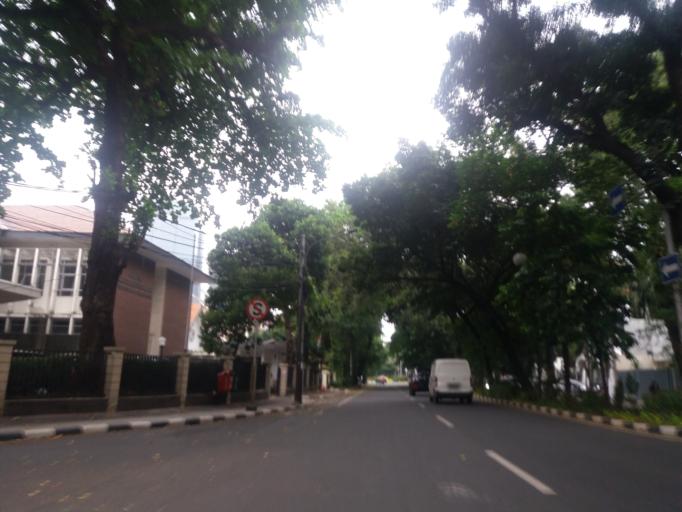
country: ID
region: Jakarta Raya
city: Jakarta
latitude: -6.1897
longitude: 106.8331
